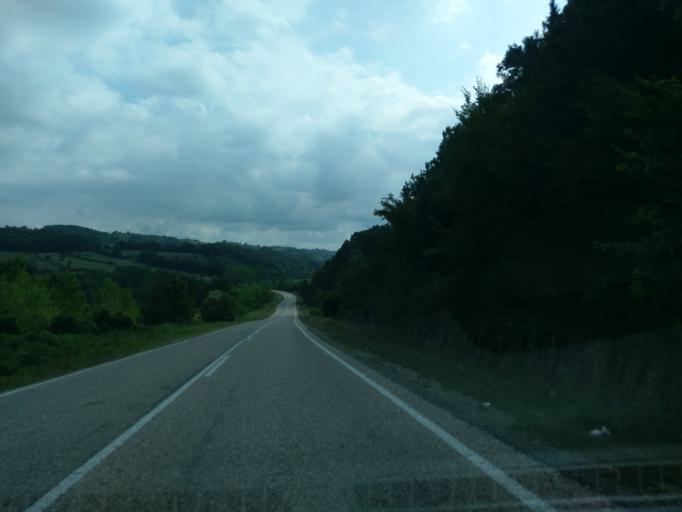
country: TR
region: Sinop
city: Erfelek
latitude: 41.9598
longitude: 34.8294
